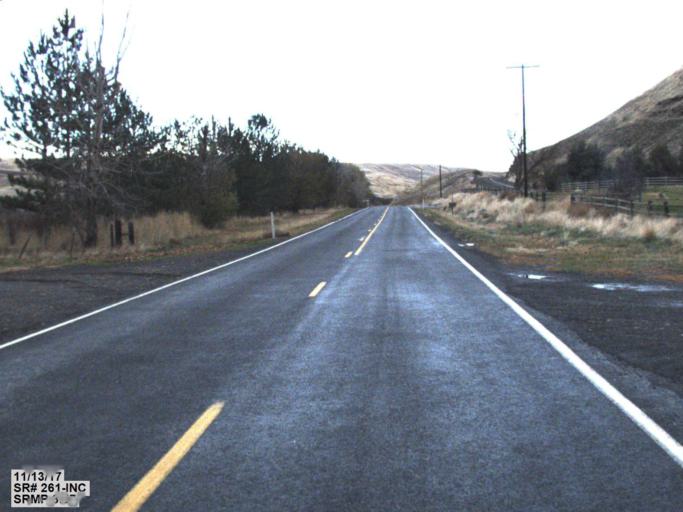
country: US
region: Washington
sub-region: Walla Walla County
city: Waitsburg
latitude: 46.5255
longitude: -118.1358
